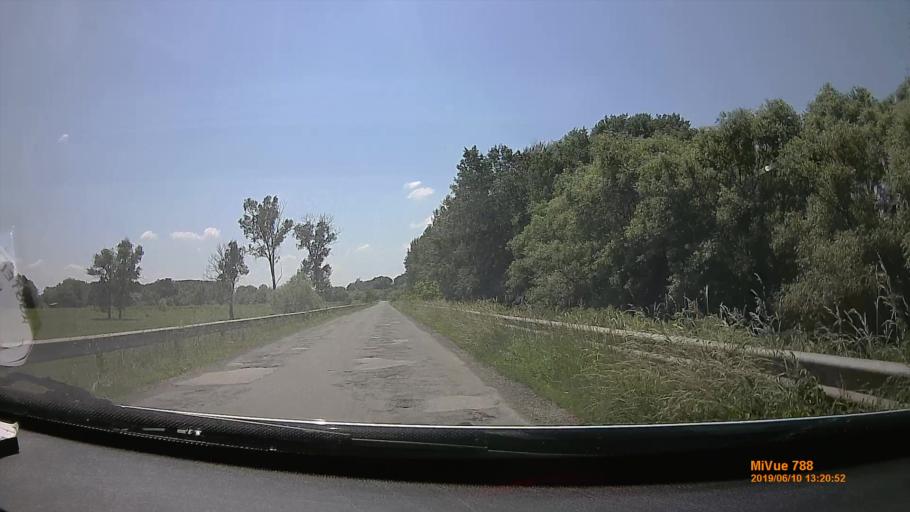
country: HU
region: Borsod-Abauj-Zemplen
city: Tiszaluc
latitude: 48.0388
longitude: 21.0798
